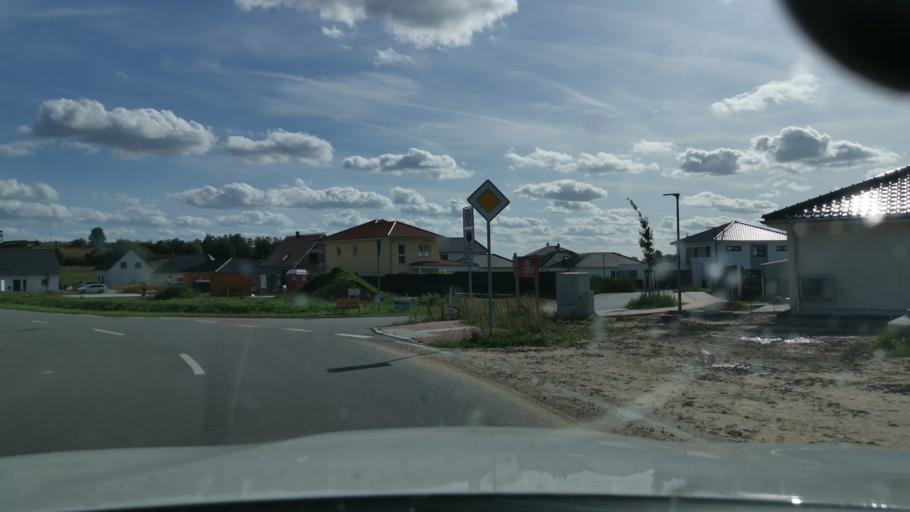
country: DE
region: Mecklenburg-Vorpommern
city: Tessin
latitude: 54.0282
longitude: 12.4499
